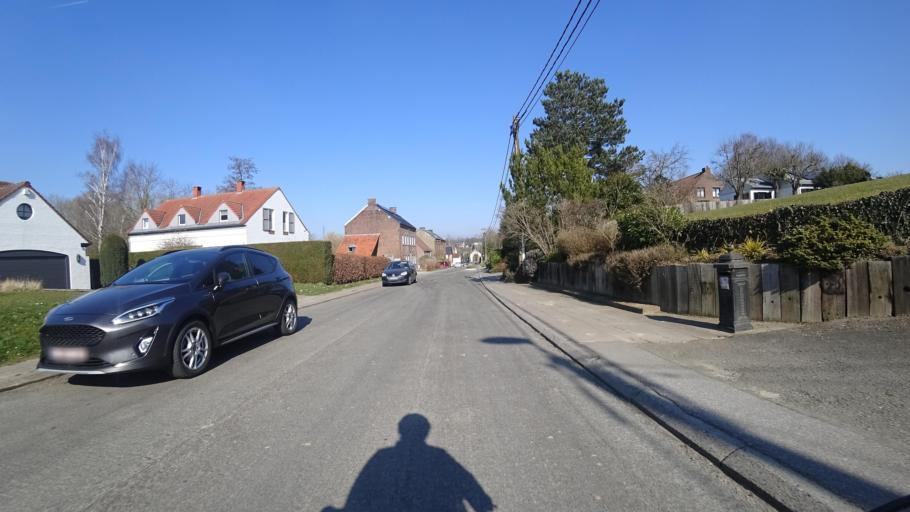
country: BE
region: Wallonia
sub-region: Province du Brabant Wallon
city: Mont-Saint-Guibert
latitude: 50.6373
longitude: 4.5945
